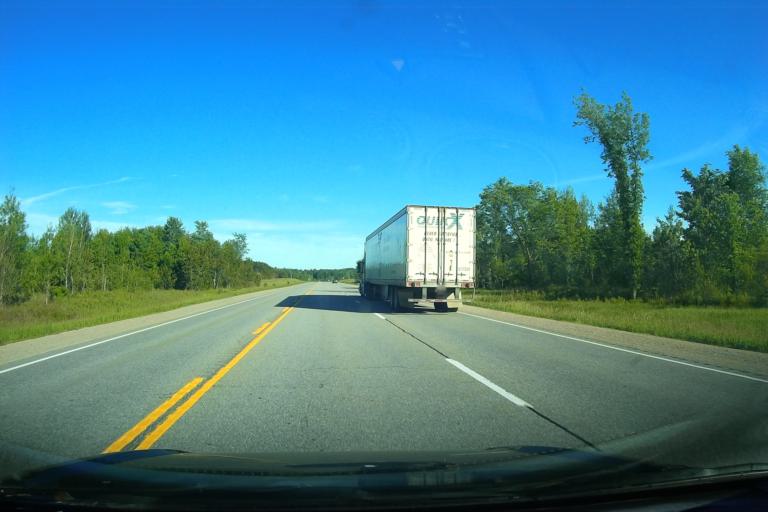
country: CA
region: Ontario
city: Renfrew
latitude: 45.5257
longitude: -76.6907
